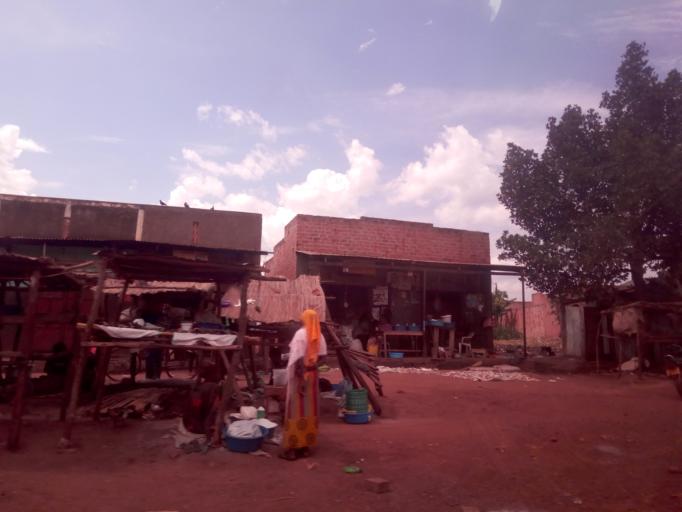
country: UG
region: Western Region
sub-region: Masindi District
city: Masindi
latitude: 1.6799
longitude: 31.7331
